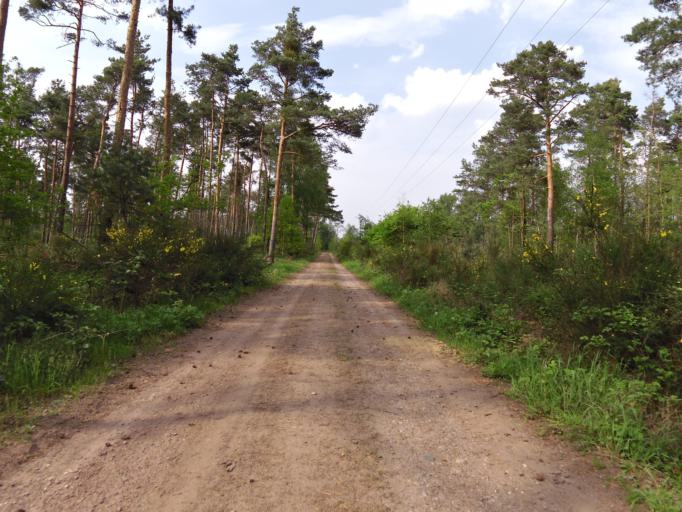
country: DE
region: Rheinland-Pfalz
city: Lachen-Speyerdorf
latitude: 49.3480
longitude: 8.2277
